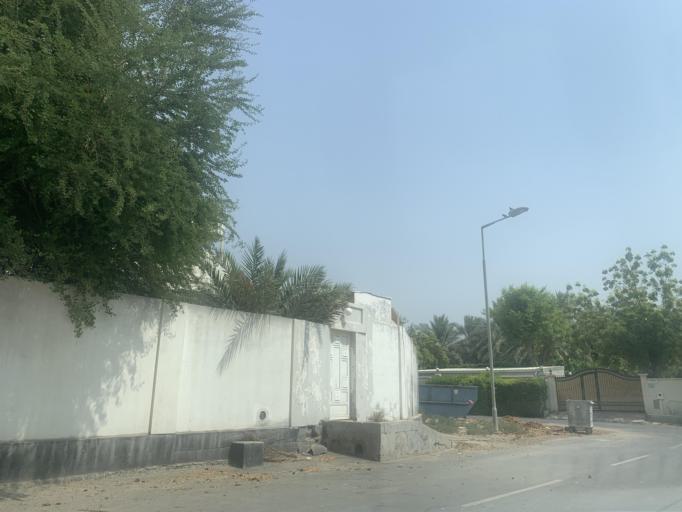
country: BH
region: Central Governorate
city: Madinat Hamad
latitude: 26.1625
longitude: 50.4498
